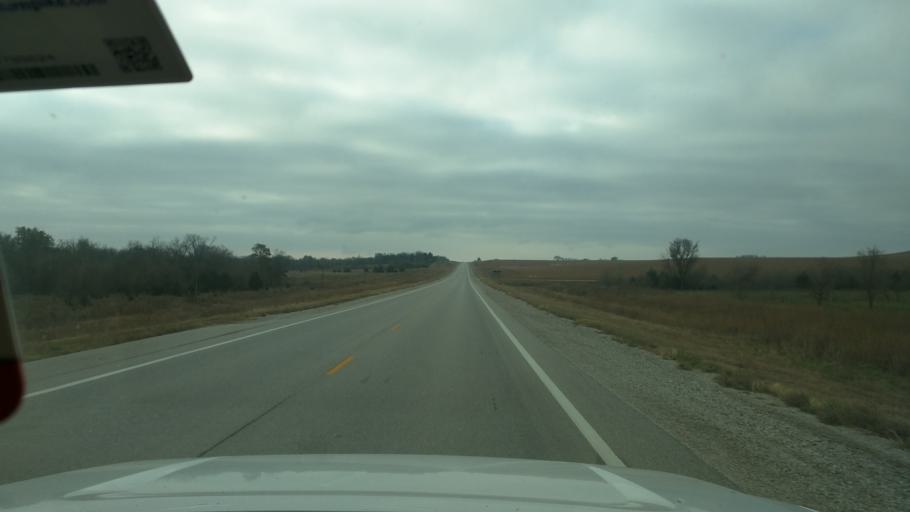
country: US
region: Kansas
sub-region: Elk County
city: Howard
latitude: 37.5942
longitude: -96.2534
